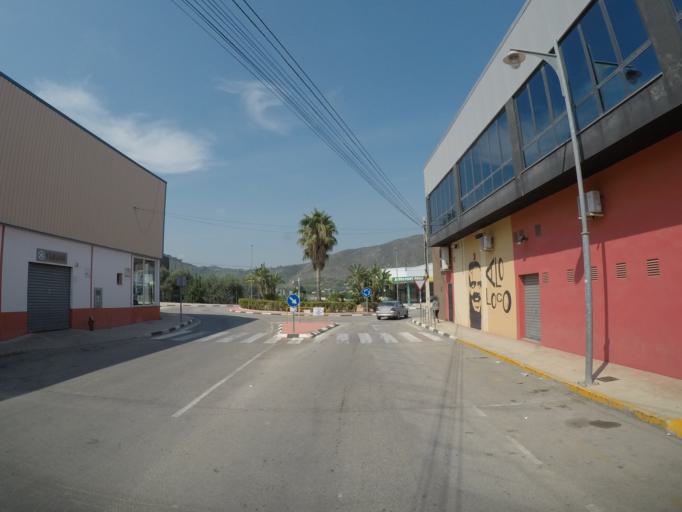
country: ES
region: Valencia
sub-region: Provincia de Alicante
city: Pego
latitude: 38.8478
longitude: -0.1140
